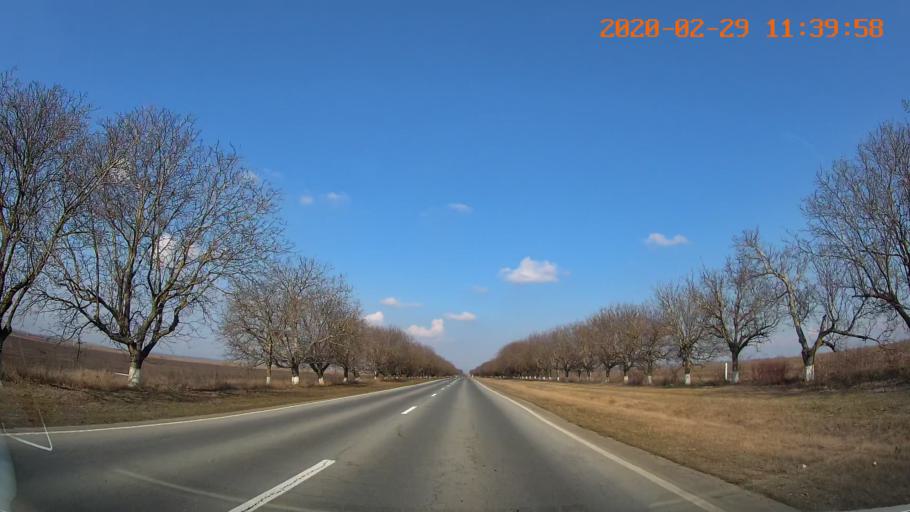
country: MD
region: Rezina
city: Saharna
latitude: 47.6487
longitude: 29.0221
